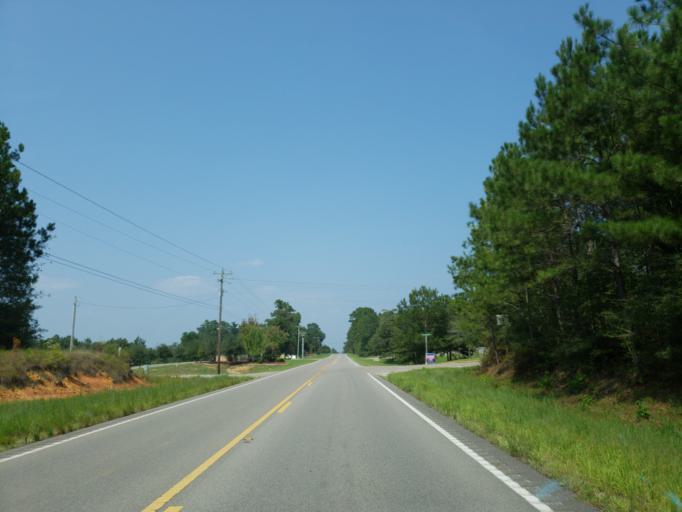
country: US
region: Mississippi
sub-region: Jones County
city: Ellisville
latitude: 31.5500
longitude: -89.2533
